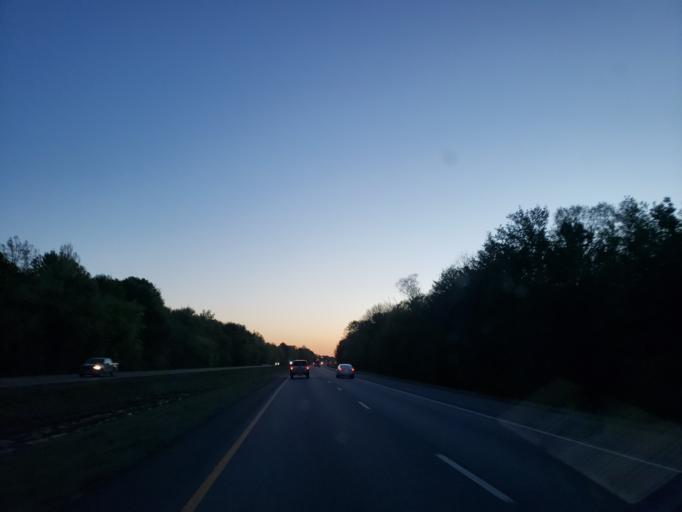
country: US
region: Alabama
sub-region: Tuscaloosa County
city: Tuscaloosa
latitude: 33.1620
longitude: -87.5759
